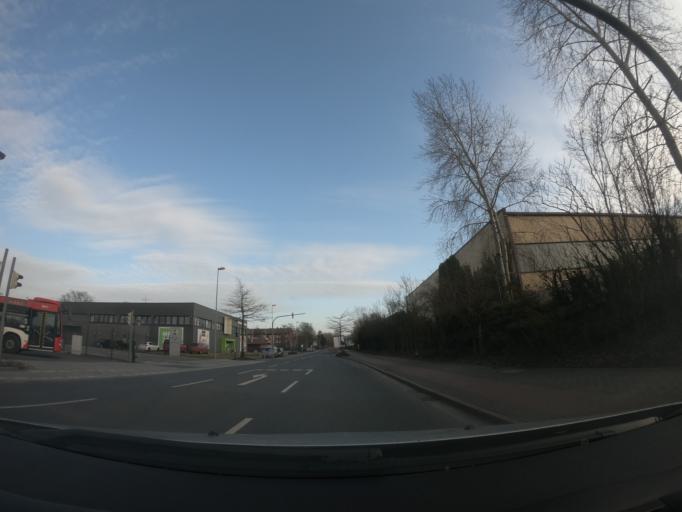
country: DE
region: North Rhine-Westphalia
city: Lunen
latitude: 51.6063
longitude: 7.5124
